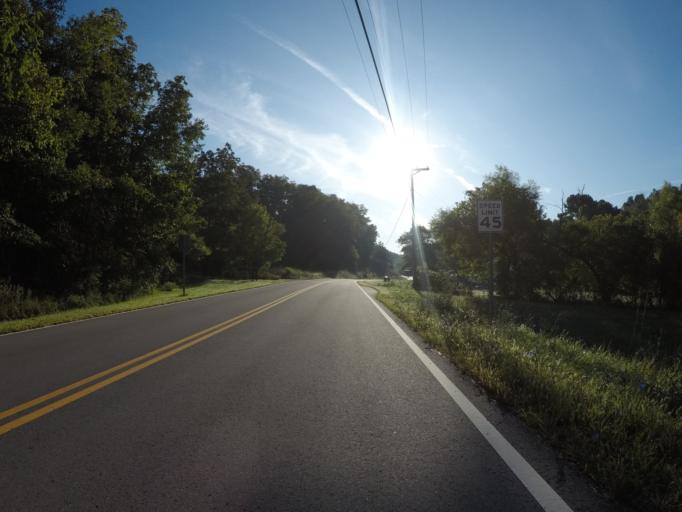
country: US
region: Ohio
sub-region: Lawrence County
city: Coal Grove
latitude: 38.6061
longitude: -82.5832
